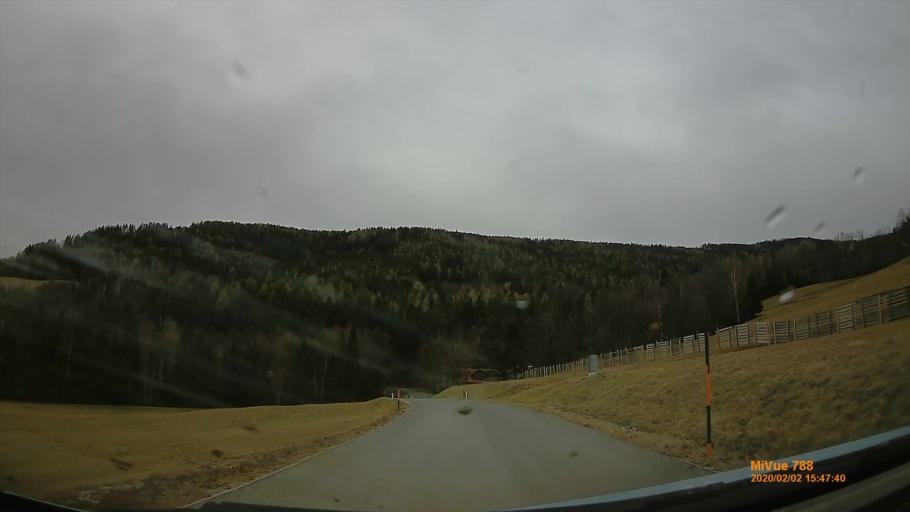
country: AT
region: Lower Austria
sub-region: Politischer Bezirk Neunkirchen
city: Reichenau an der Rax
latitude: 47.6878
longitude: 15.8149
